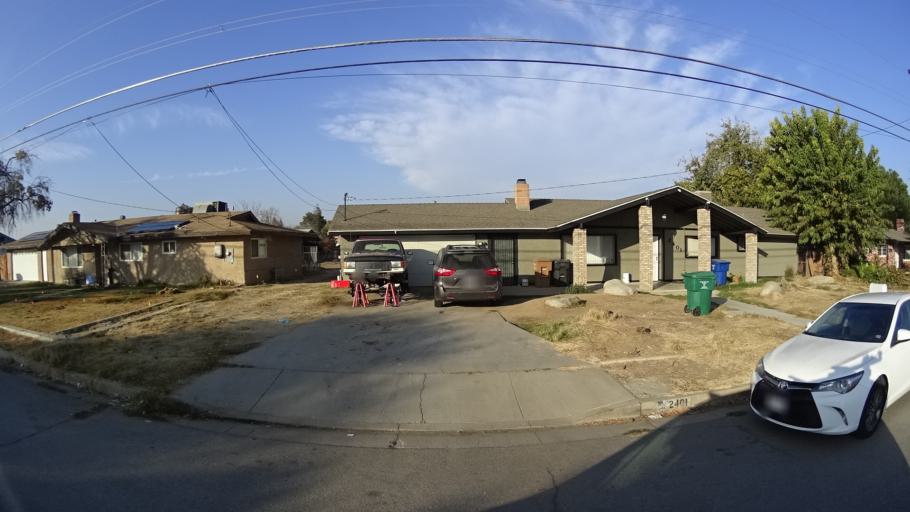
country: US
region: California
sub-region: Kern County
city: Greenacres
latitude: 35.3818
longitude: -119.1190
